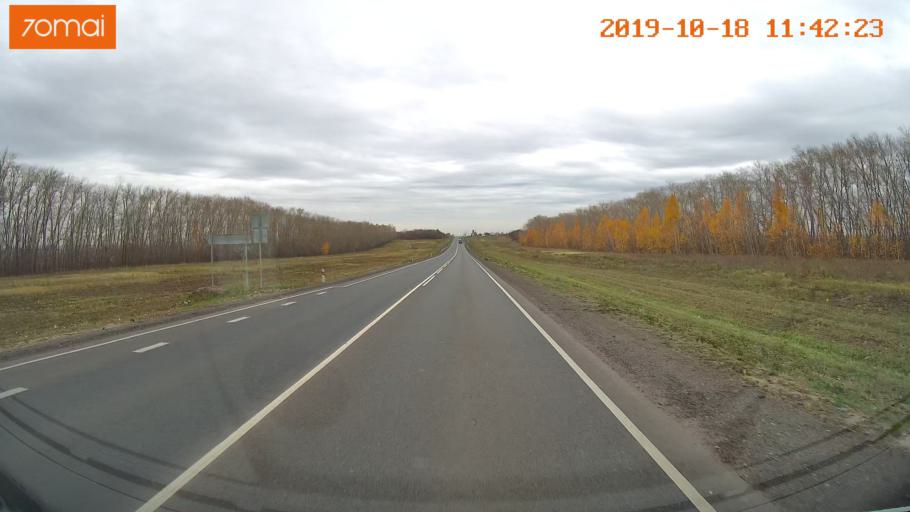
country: RU
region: Rjazan
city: Oktyabr'skiy
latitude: 54.1876
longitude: 38.9265
